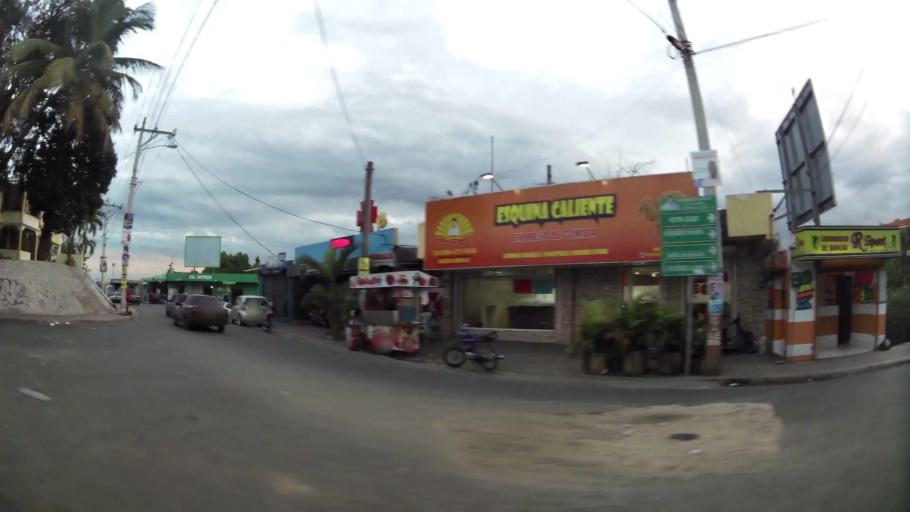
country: DO
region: Santo Domingo
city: Santo Domingo Oeste
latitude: 18.5238
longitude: -70.0218
